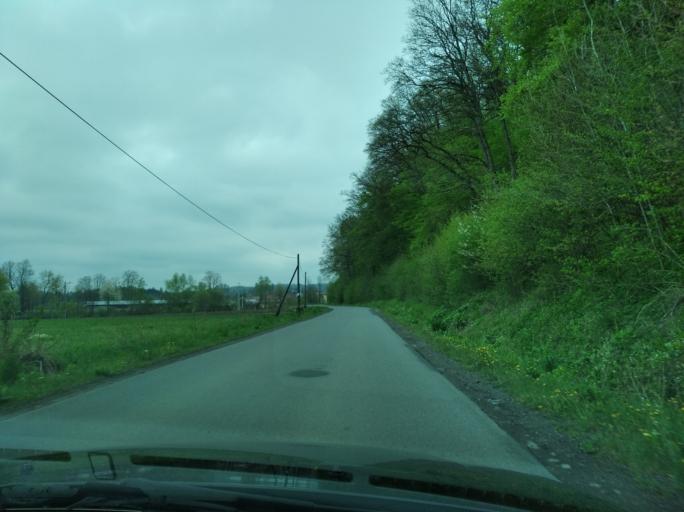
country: PL
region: Subcarpathian Voivodeship
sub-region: Powiat sanocki
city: Sanok
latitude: 49.5960
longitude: 22.1899
